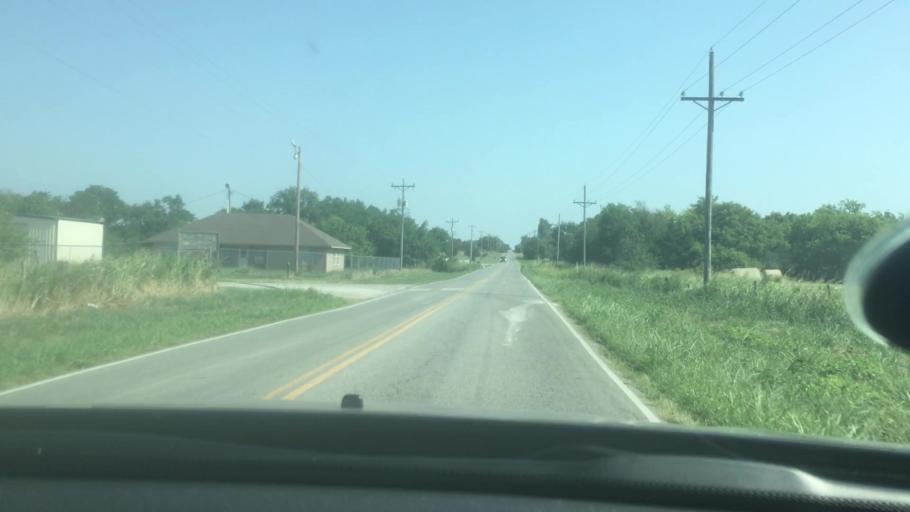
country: US
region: Oklahoma
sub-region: Bryan County
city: Calera
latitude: 34.0014
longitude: -96.4656
